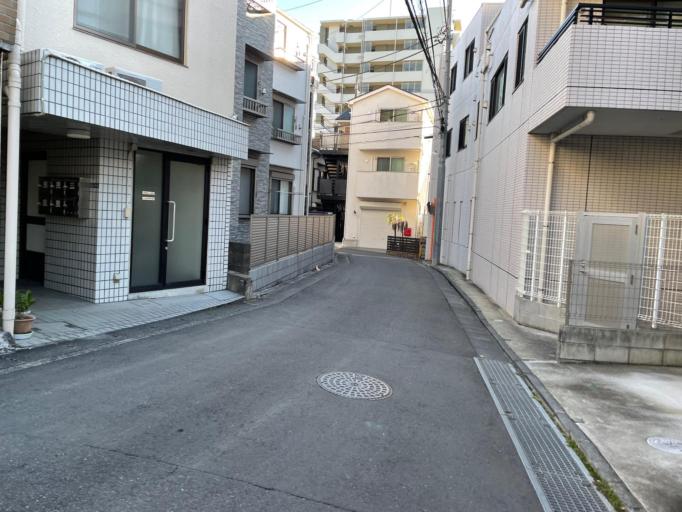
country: JP
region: Tokyo
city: Chofugaoka
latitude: 35.6155
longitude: 139.5262
